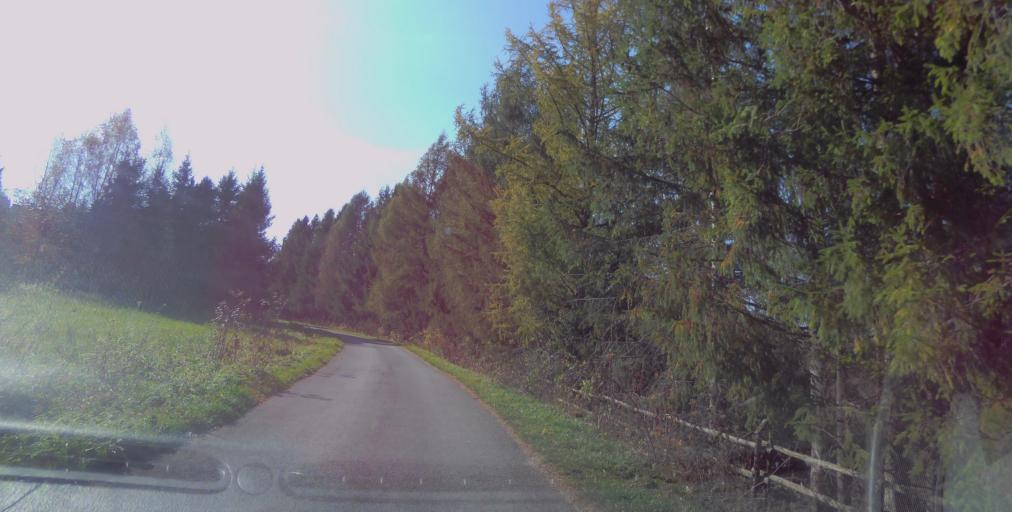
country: PL
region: Subcarpathian Voivodeship
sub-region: Powiat leski
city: Polanczyk
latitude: 49.3285
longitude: 22.4277
